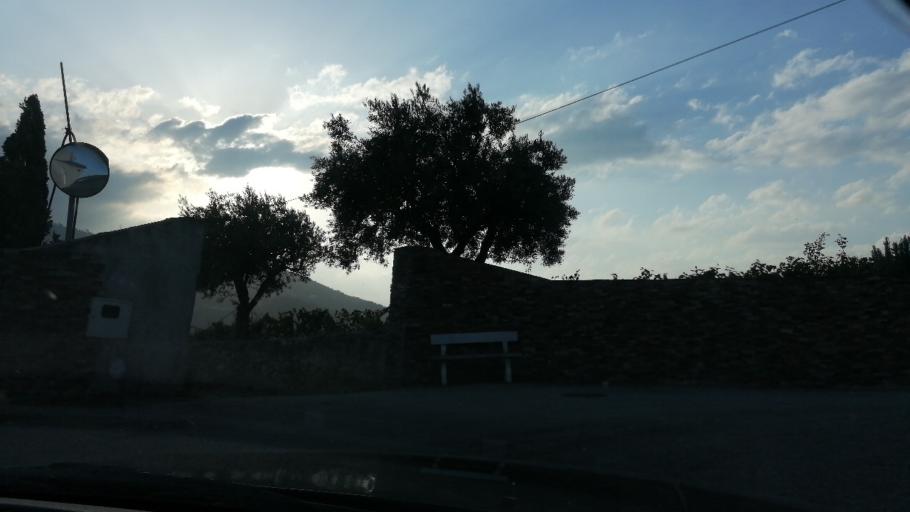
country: PT
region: Vila Real
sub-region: Peso da Regua
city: Godim
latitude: 41.1519
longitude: -7.8156
